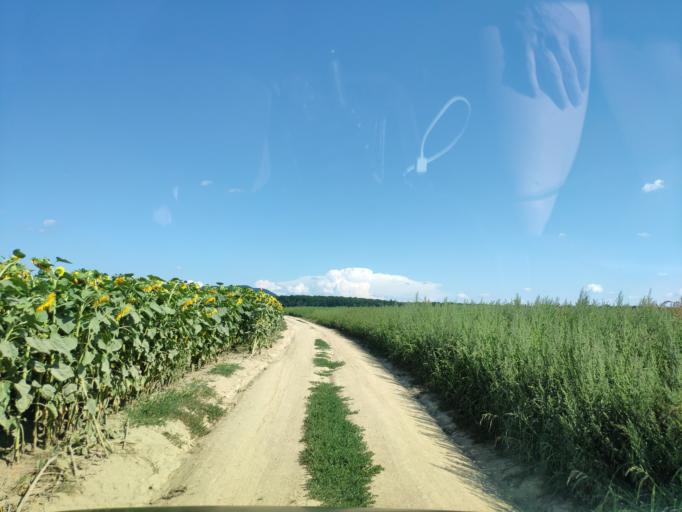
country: SK
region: Presovsky
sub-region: Okres Presov
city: Presov
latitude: 48.9075
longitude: 21.2718
